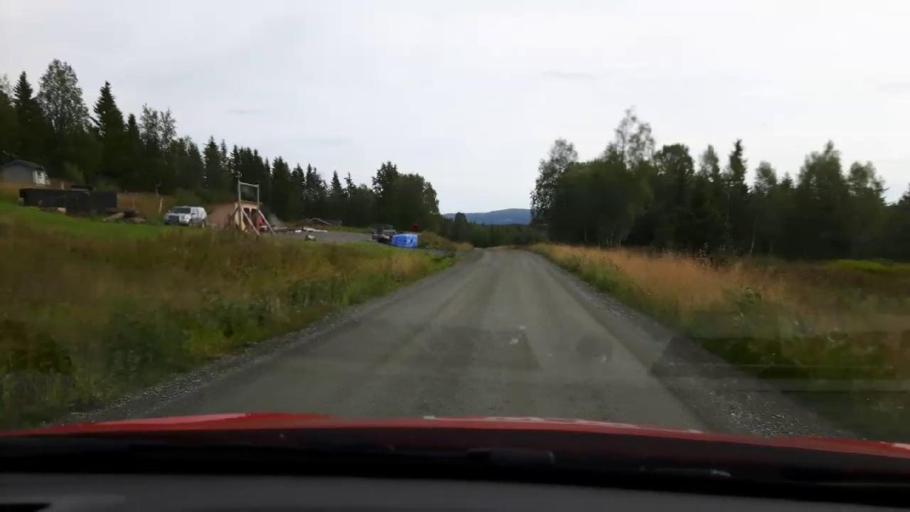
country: SE
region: Jaemtland
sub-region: Are Kommun
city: Are
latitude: 63.7453
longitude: 12.9764
